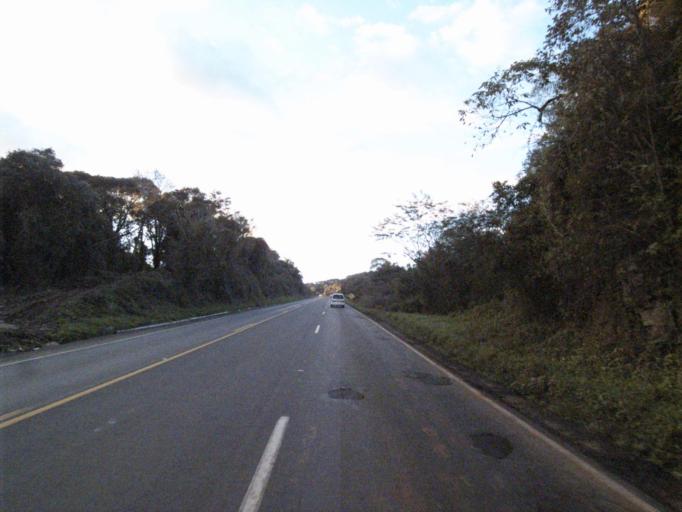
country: BR
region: Santa Catarina
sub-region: Joacaba
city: Joacaba
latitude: -27.1865
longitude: -51.5186
